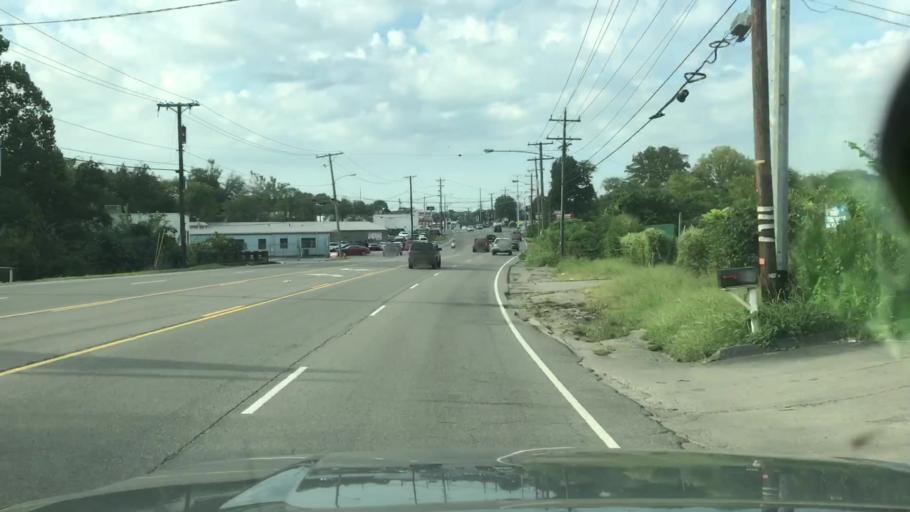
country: US
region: Tennessee
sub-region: Davidson County
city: Nashville
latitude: 36.2102
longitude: -86.7659
